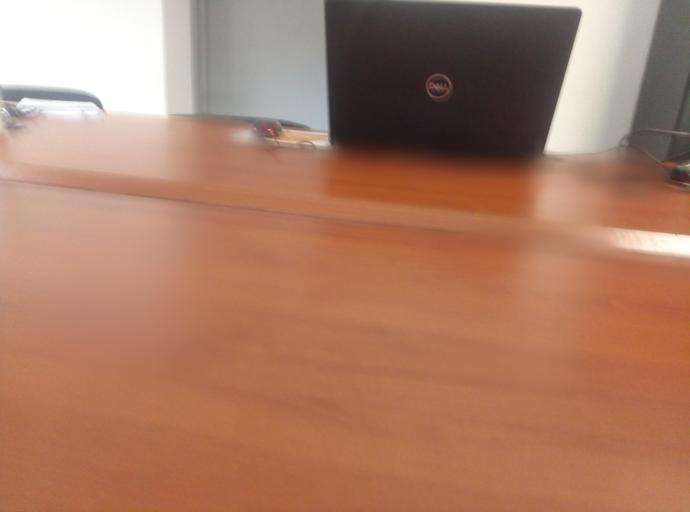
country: MG
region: Analamanga
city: Antananarivo
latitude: -18.8723
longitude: 47.5260
